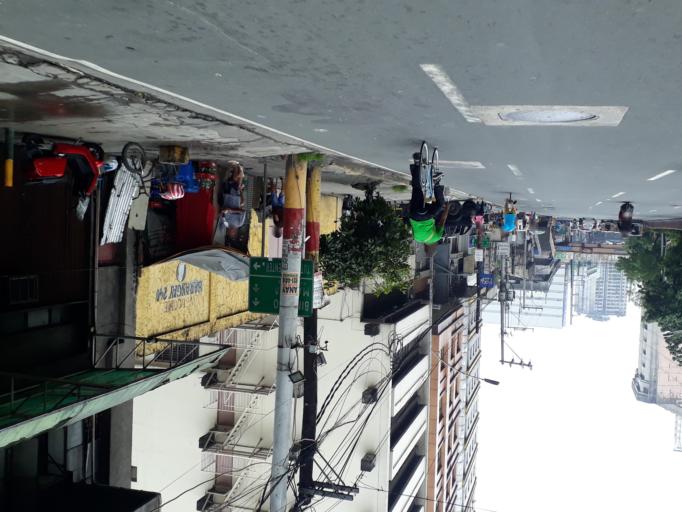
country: PH
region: Metro Manila
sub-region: City of Manila
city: Manila
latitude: 14.6074
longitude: 120.9753
